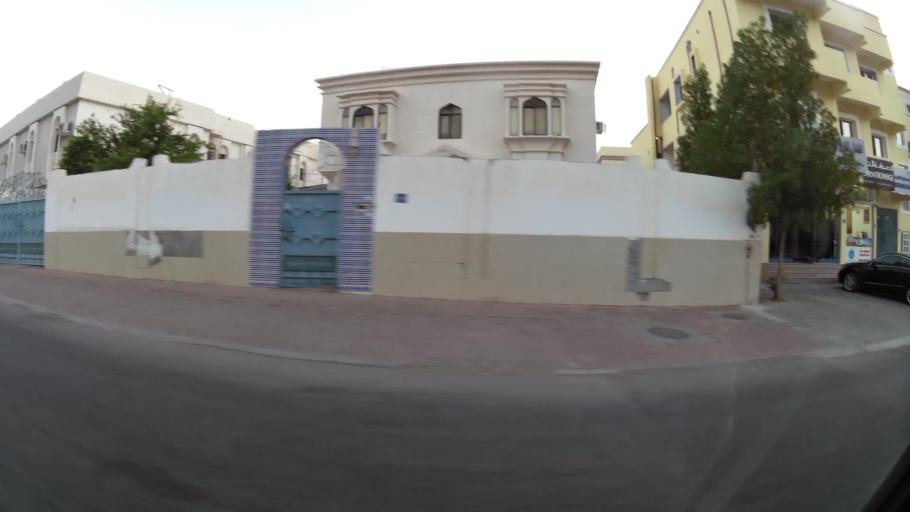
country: OM
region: Muhafazat Masqat
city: Muscat
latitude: 23.5863
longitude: 58.5640
